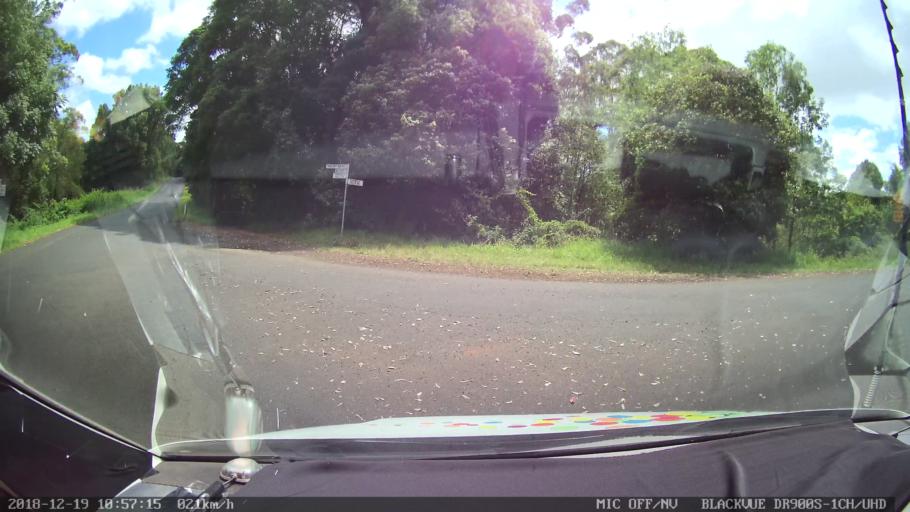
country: AU
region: New South Wales
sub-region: Lismore Municipality
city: Nimbin
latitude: -28.5891
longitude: 153.2614
